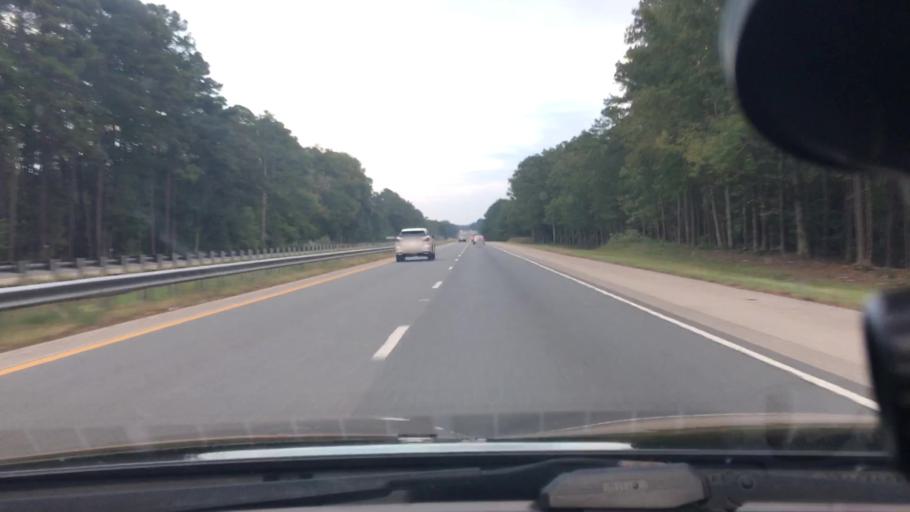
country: US
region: North Carolina
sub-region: Chatham County
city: Pittsboro
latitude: 35.6298
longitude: -79.0698
